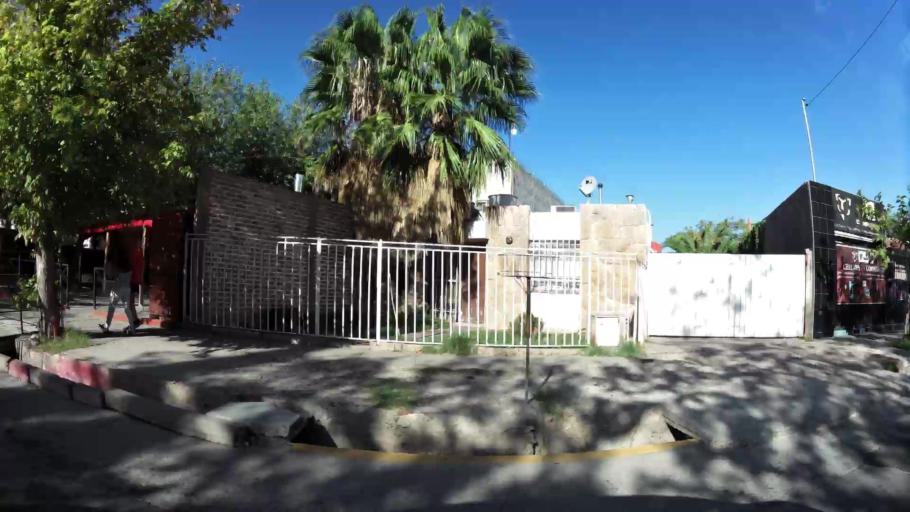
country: AR
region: Mendoza
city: Villa Nueva
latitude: -32.9057
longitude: -68.8002
